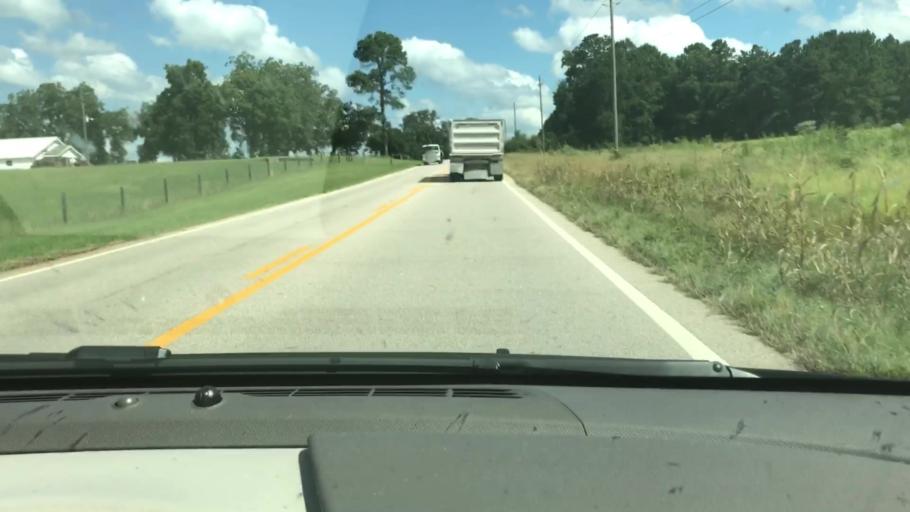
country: US
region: Georgia
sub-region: Troup County
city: West Point
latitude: 32.8765
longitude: -85.0342
